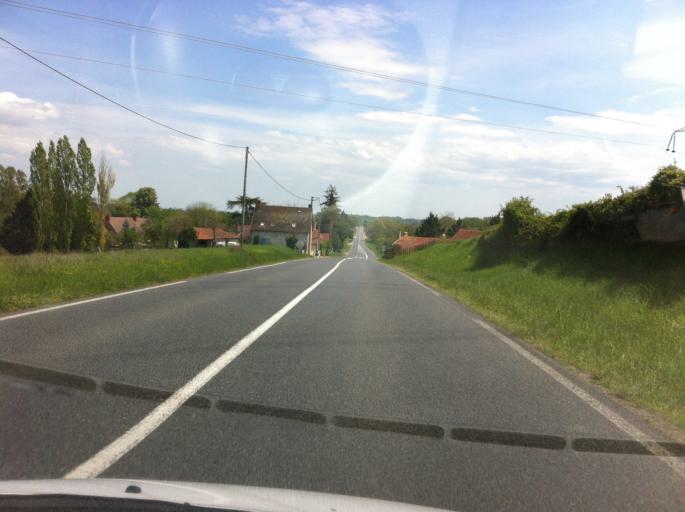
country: FR
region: Auvergne
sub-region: Departement de l'Allier
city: Saint-Pourcain-sur-Sioule
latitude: 46.3160
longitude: 3.2560
